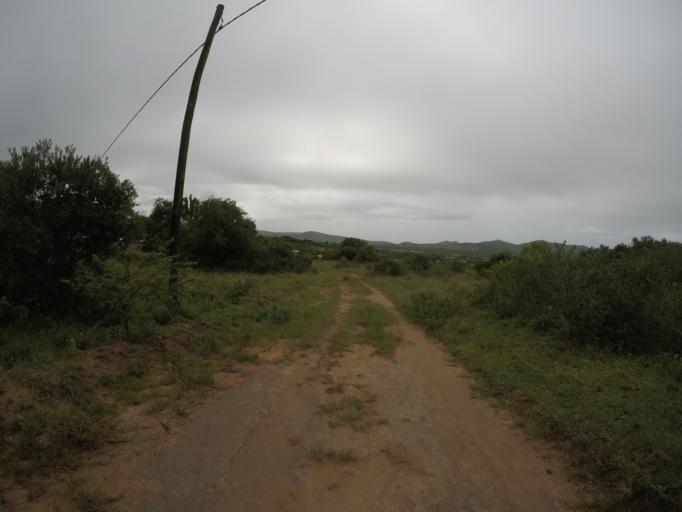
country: ZA
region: KwaZulu-Natal
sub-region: uThungulu District Municipality
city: Empangeni
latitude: -28.6092
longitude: 31.8409
